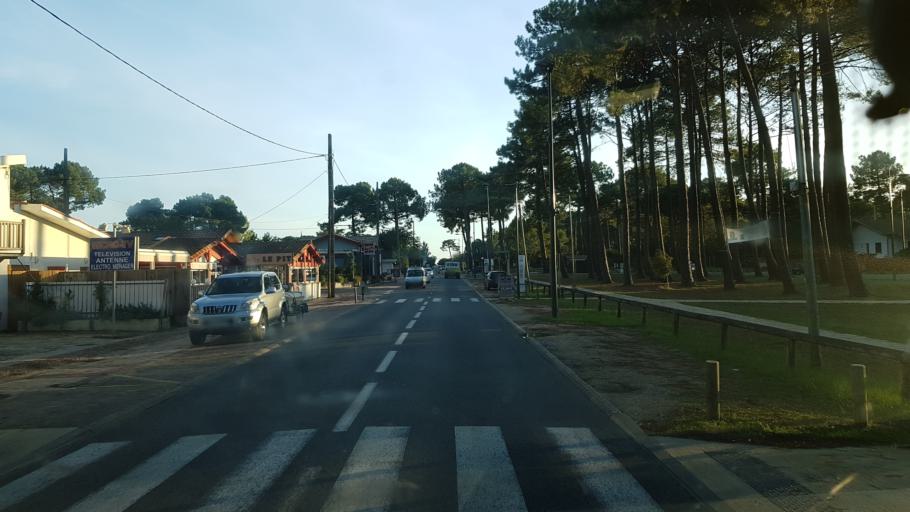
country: FR
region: Aquitaine
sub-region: Departement de la Gironde
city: Ares
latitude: 44.7493
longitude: -1.1809
